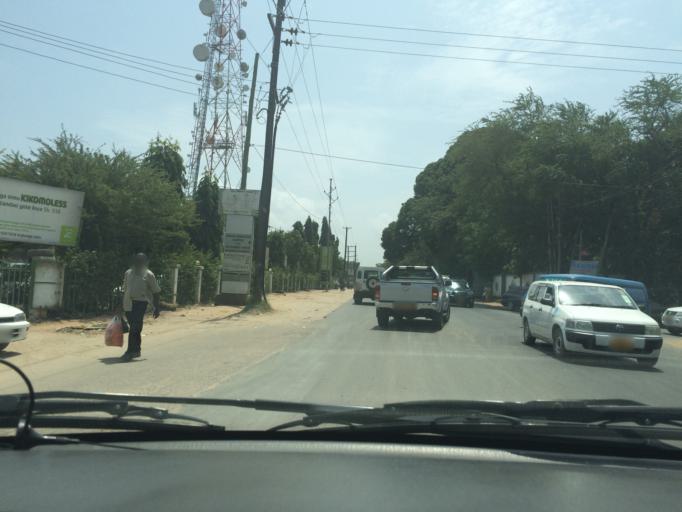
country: TZ
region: Dar es Salaam
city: Magomeni
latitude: -6.7714
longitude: 39.2642
